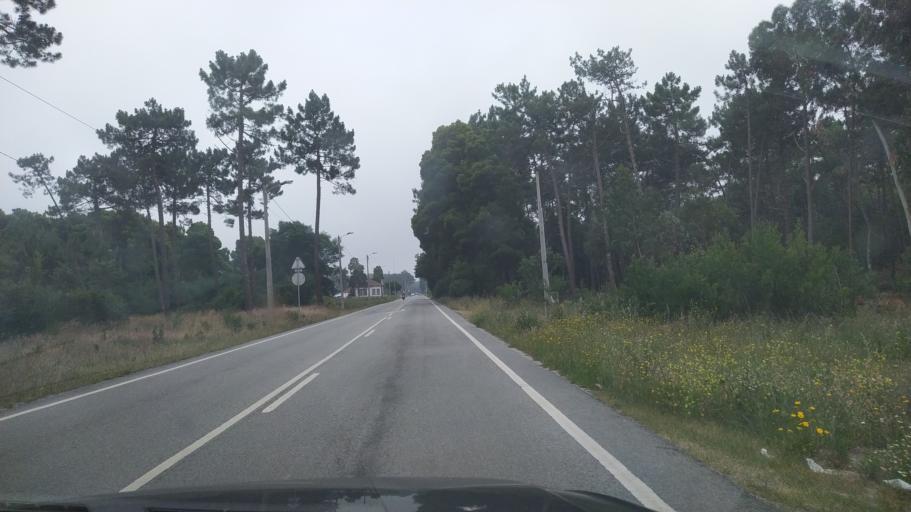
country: PT
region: Aveiro
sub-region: Ilhavo
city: Gafanha da Encarnacao
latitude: 40.6058
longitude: -8.7220
